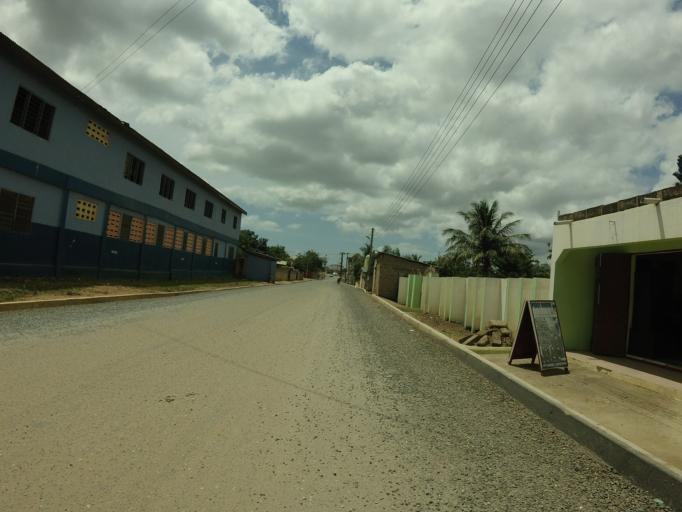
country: GH
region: Central
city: Kasoa
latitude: 5.5456
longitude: -0.3985
